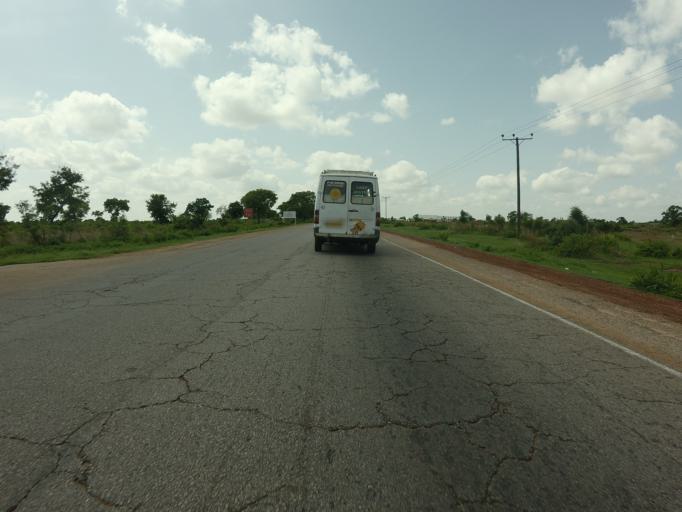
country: GH
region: Northern
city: Savelugu
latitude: 9.5826
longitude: -0.8335
